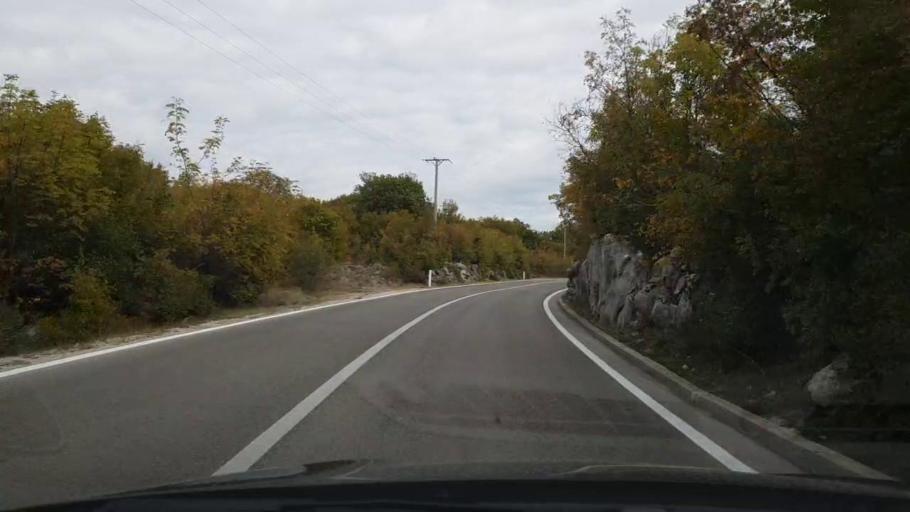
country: BA
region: Republika Srpska
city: Trebinje
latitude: 42.6893
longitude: 18.2547
